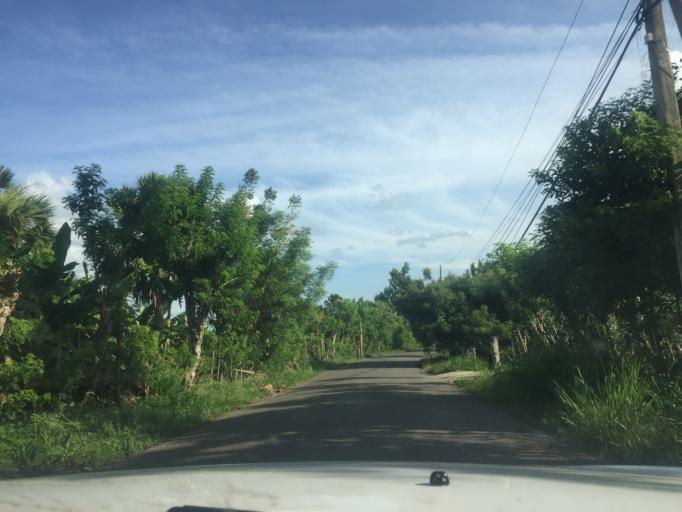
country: DO
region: Santiago
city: Tamboril
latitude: 19.4952
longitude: -70.6348
